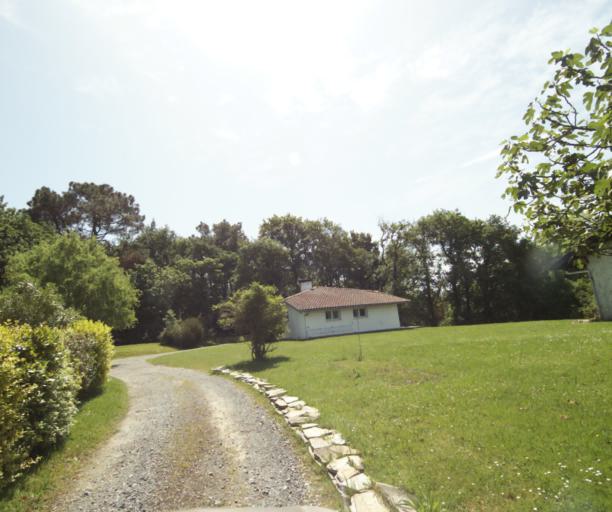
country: FR
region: Aquitaine
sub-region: Departement des Pyrenees-Atlantiques
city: Mouguerre
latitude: 43.4561
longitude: -1.4287
